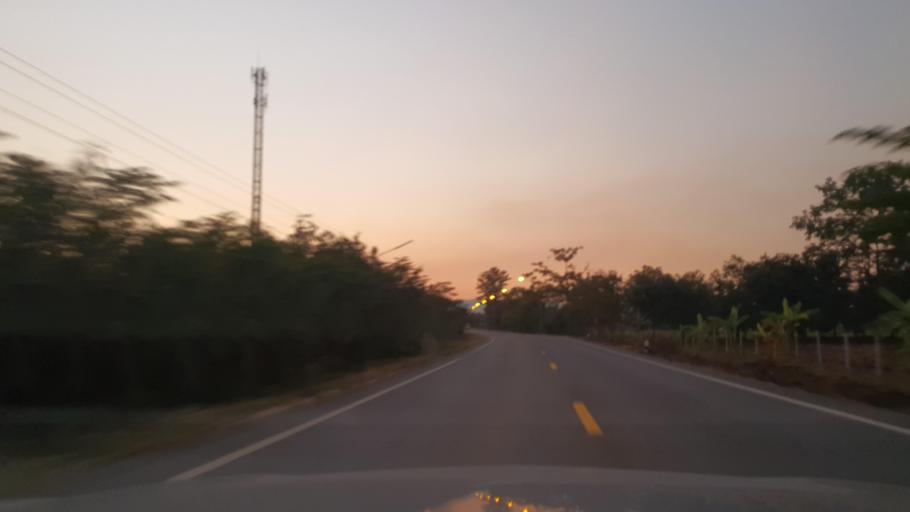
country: TH
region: Phayao
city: Dok Kham Tai
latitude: 19.1479
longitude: 100.0039
